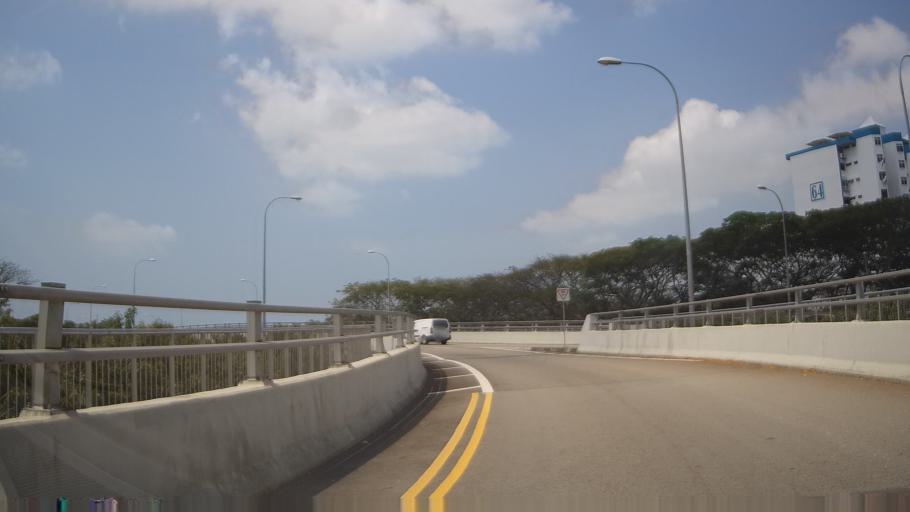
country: SG
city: Singapore
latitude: 1.3027
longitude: 103.9109
